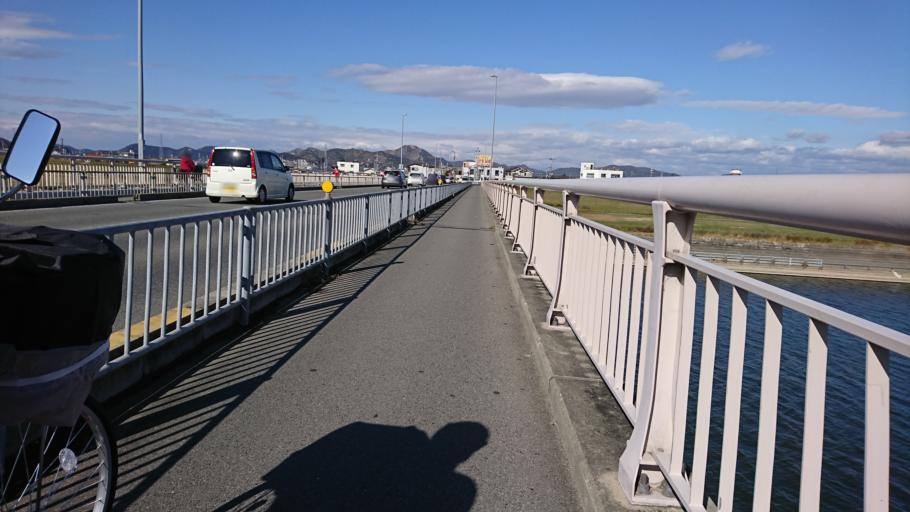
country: JP
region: Hyogo
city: Kakogawacho-honmachi
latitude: 34.7727
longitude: 134.8283
